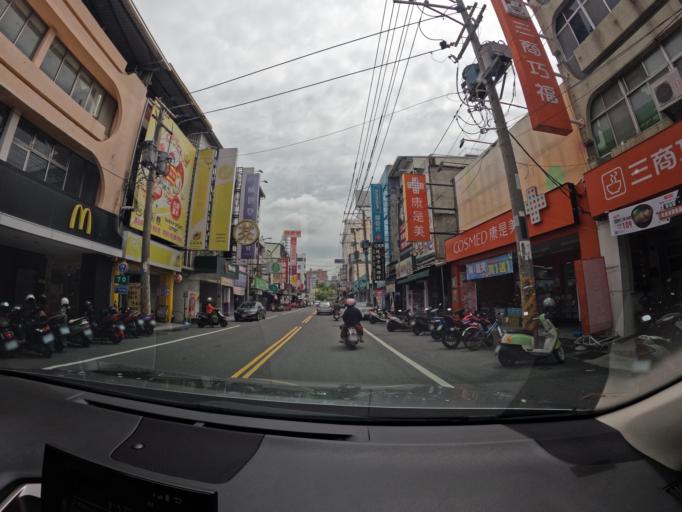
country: TW
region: Kaohsiung
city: Kaohsiung
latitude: 22.7944
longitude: 120.2909
